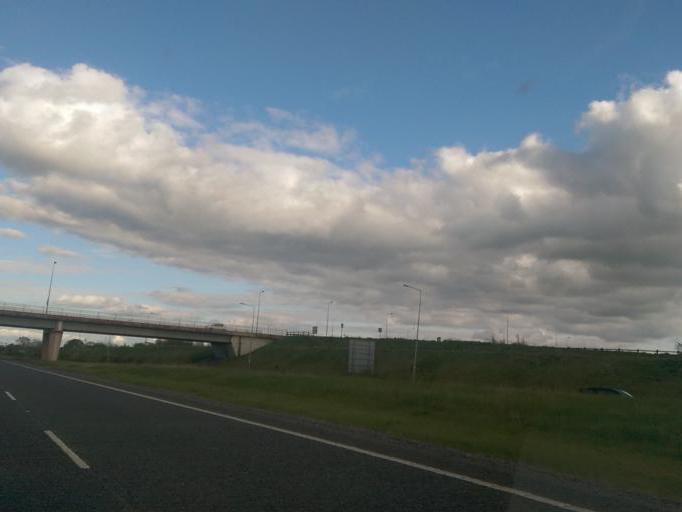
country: IE
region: Leinster
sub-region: An Iarmhi
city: Kinnegad
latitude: 53.4494
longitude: -7.0951
